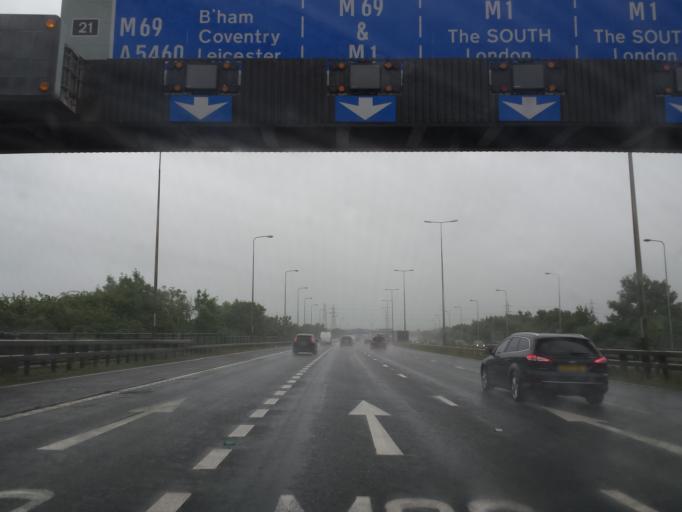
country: GB
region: England
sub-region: Leicestershire
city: Enderby
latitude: 52.6075
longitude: -1.1973
